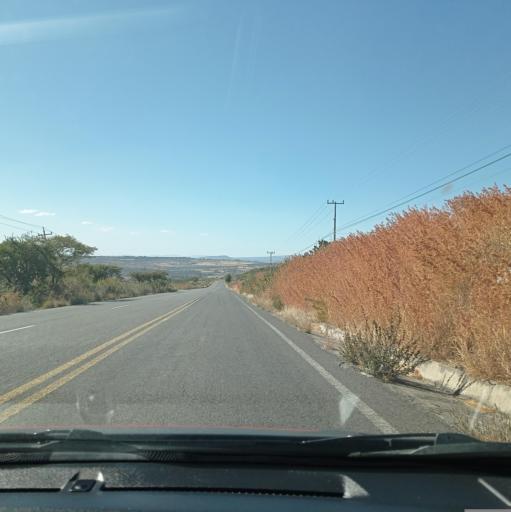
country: MX
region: Jalisco
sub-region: San Julian
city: Colonia Veintitres de Mayo
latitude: 21.0087
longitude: -102.2617
